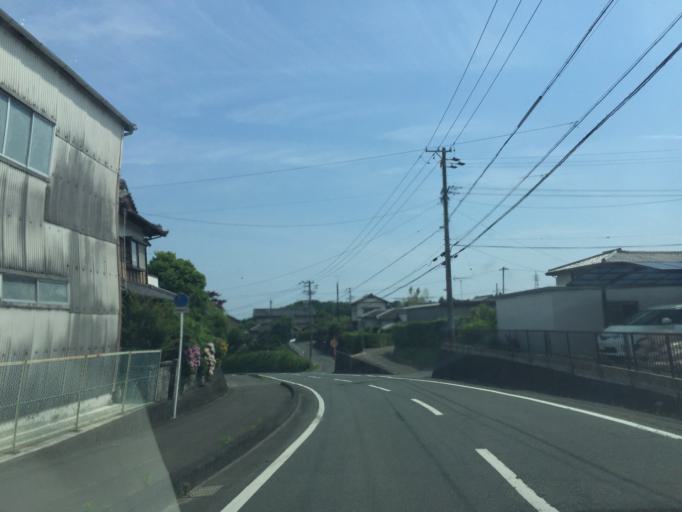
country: JP
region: Shizuoka
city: Fukuroi
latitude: 34.7852
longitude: 137.9505
